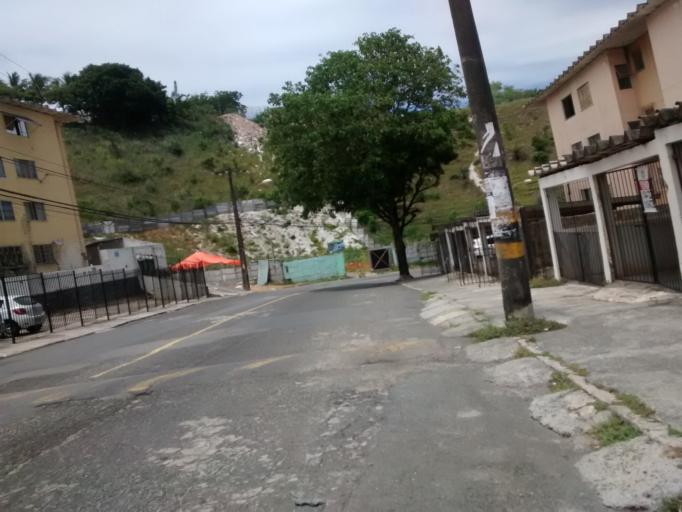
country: BR
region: Bahia
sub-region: Salvador
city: Salvador
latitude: -12.9754
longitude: -38.4403
